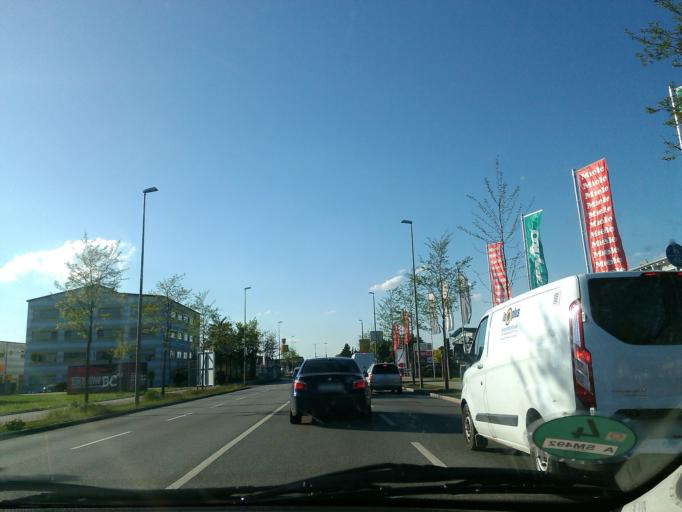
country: DE
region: Bavaria
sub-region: Swabia
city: Augsburg
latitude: 48.3871
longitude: 10.9379
